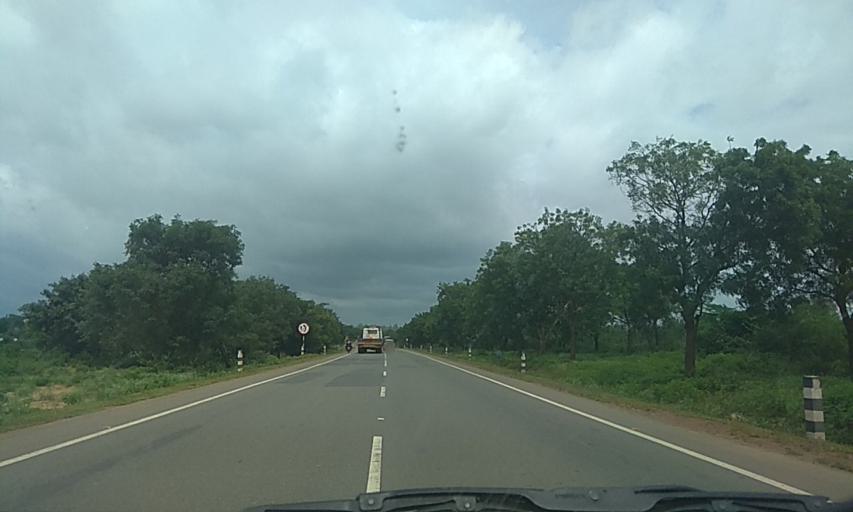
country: IN
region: Karnataka
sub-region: Dharwad
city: Hubli
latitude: 15.3331
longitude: 75.0987
